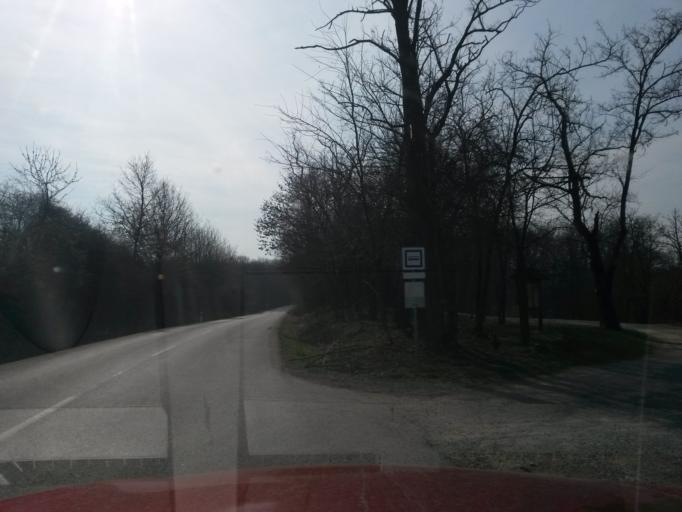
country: SK
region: Nitriansky
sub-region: Okres Nitra
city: Vrable
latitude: 48.1085
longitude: 18.4035
